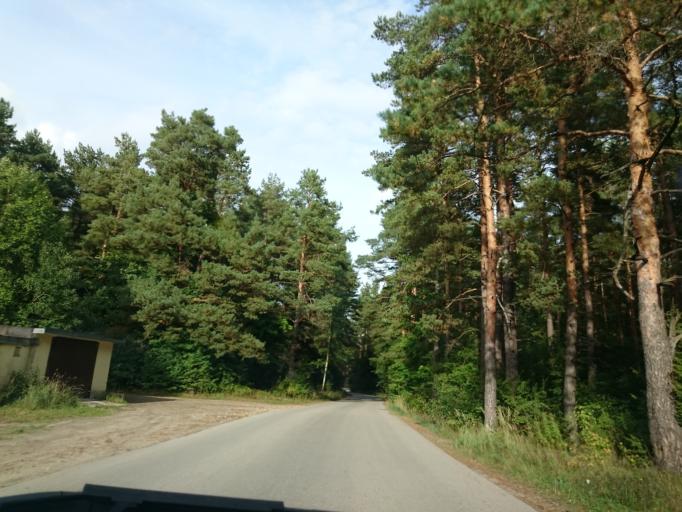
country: LV
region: Adazi
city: Adazi
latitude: 57.0375
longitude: 24.3300
